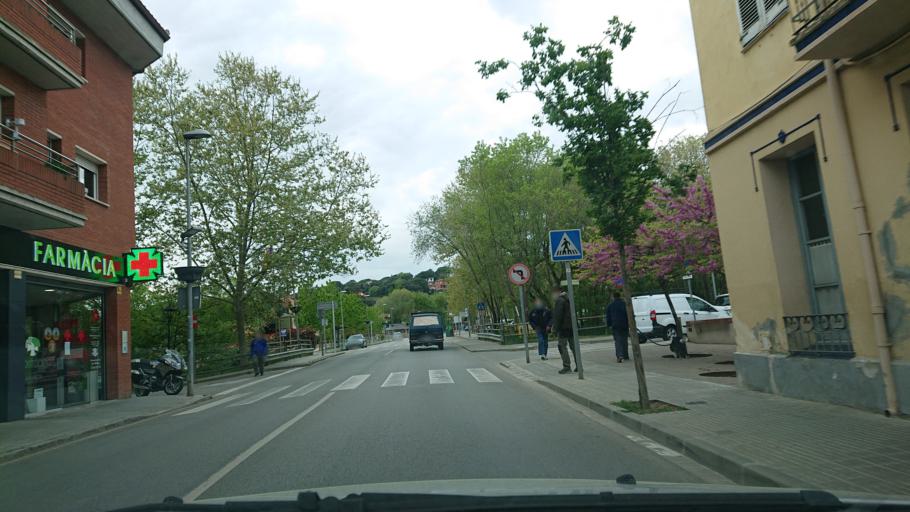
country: ES
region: Catalonia
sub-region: Provincia de Barcelona
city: Sant Pere de Vilamajor
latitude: 41.6735
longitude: 2.3990
